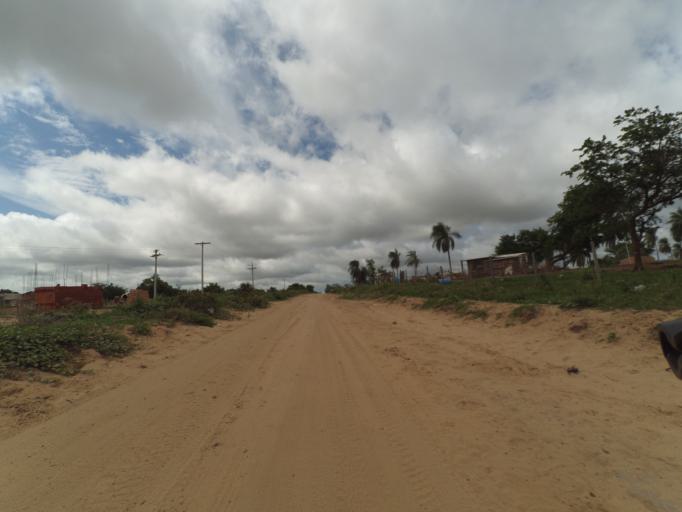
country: BO
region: Santa Cruz
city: Santa Cruz de la Sierra
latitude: -17.8800
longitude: -63.2361
